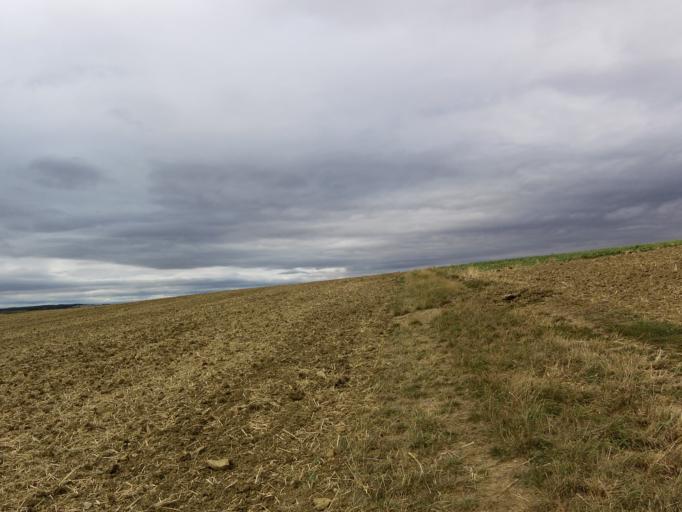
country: DE
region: Bavaria
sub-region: Regierungsbezirk Unterfranken
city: Rimpar
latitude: 49.8427
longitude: 9.9655
